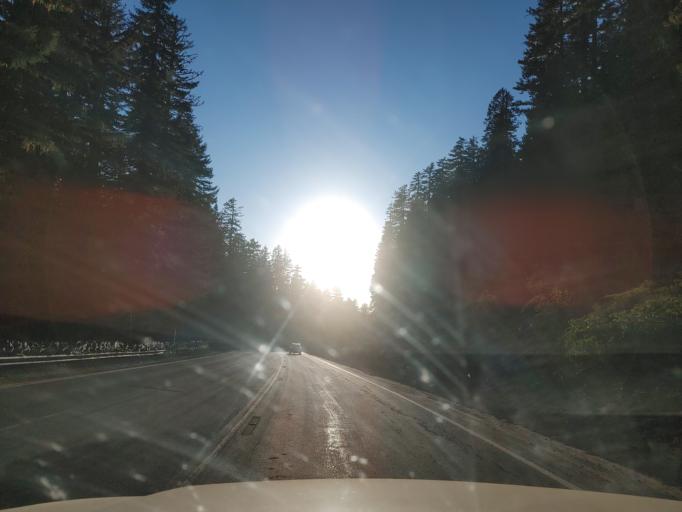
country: US
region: Oregon
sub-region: Lane County
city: Oakridge
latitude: 43.6118
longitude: -122.0615
